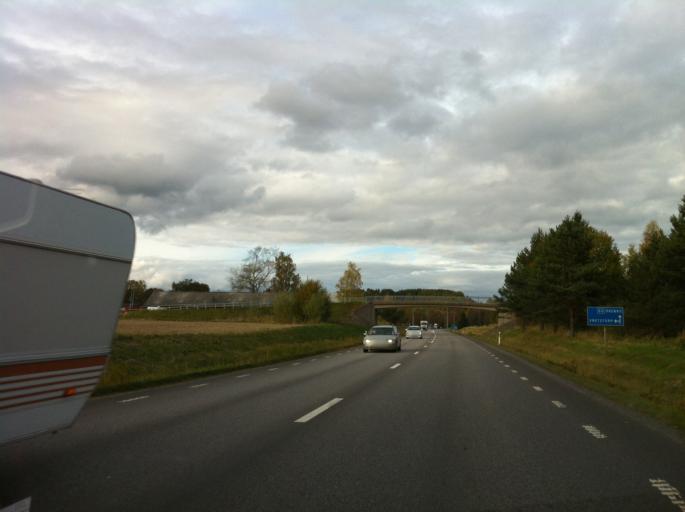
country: SE
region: OErebro
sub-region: Askersunds Kommun
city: Askersund
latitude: 58.8833
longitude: 14.8983
